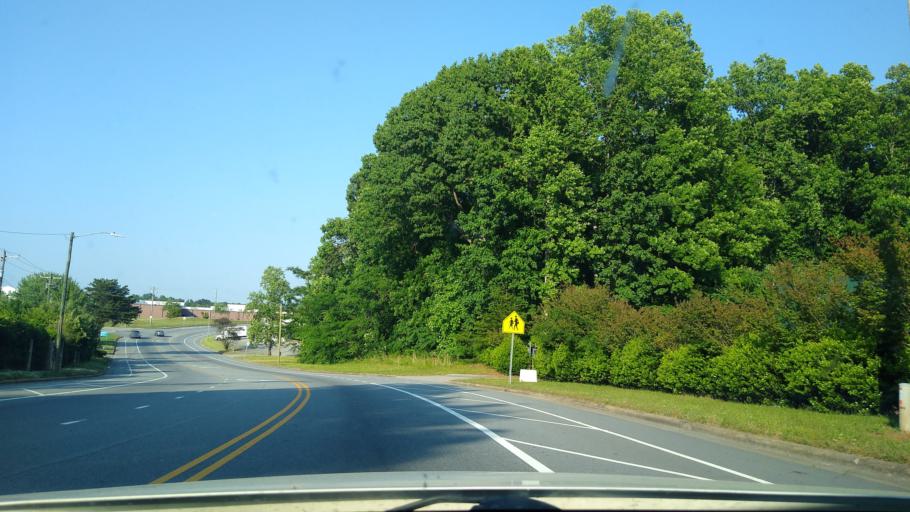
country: US
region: North Carolina
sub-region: Guilford County
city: Greensboro
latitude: 36.1064
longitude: -79.7593
